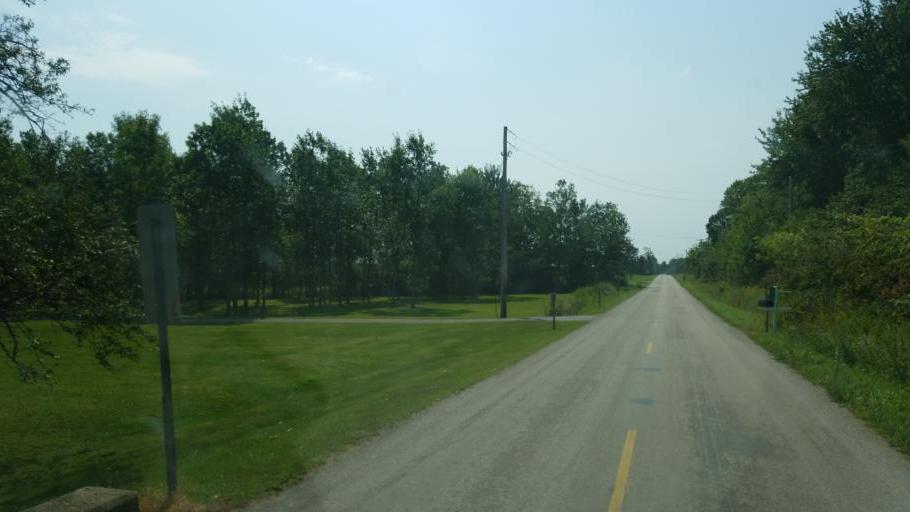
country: US
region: Ohio
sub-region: Ashtabula County
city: Orwell
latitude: 41.5959
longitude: -80.9923
